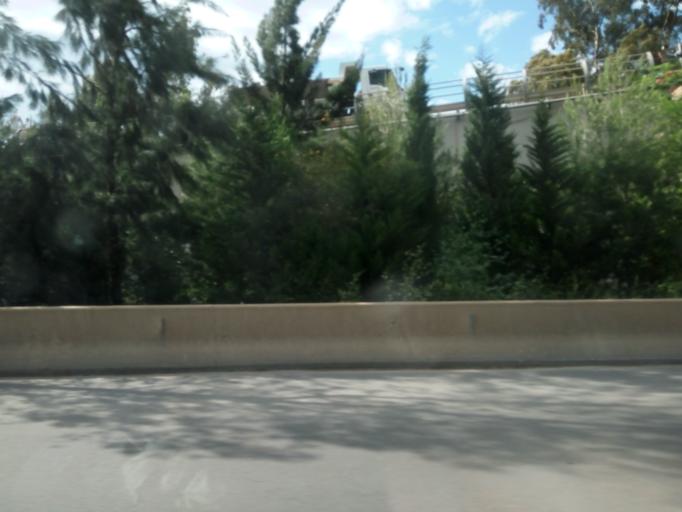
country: DZ
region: Tipaza
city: El Affroun
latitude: 36.4341
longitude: 2.5749
